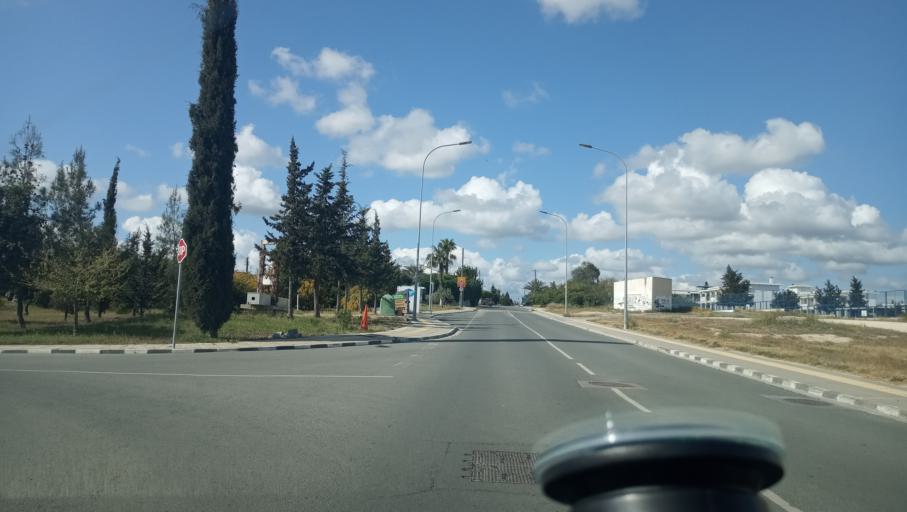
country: CY
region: Lefkosia
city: Geri
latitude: 35.1047
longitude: 33.4099
